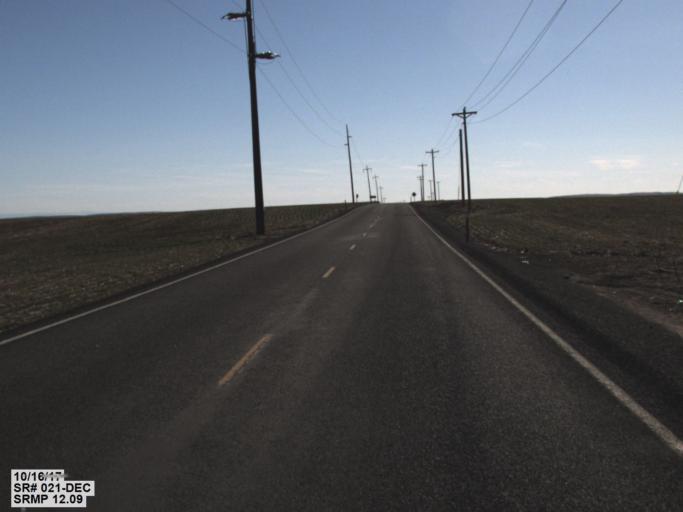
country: US
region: Washington
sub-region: Franklin County
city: Connell
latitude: 46.8014
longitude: -118.5473
